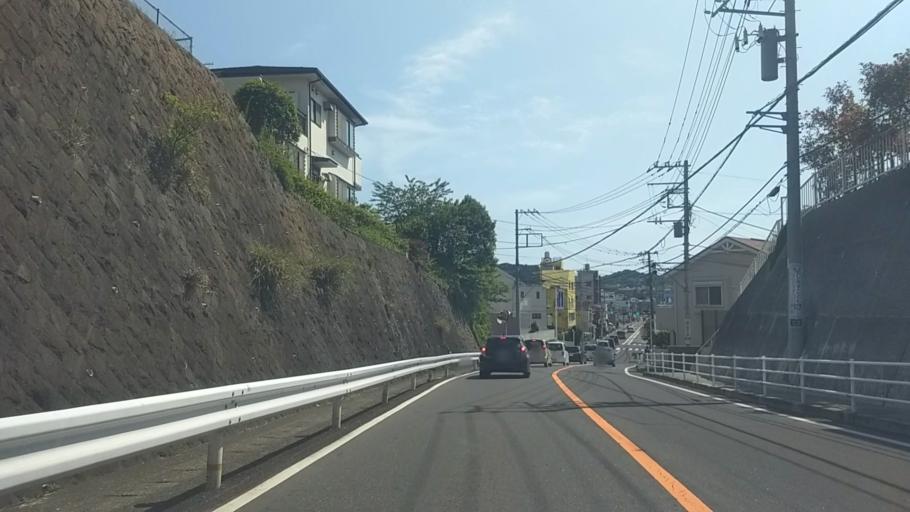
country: JP
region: Kanagawa
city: Kamakura
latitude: 35.3475
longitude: 139.5424
